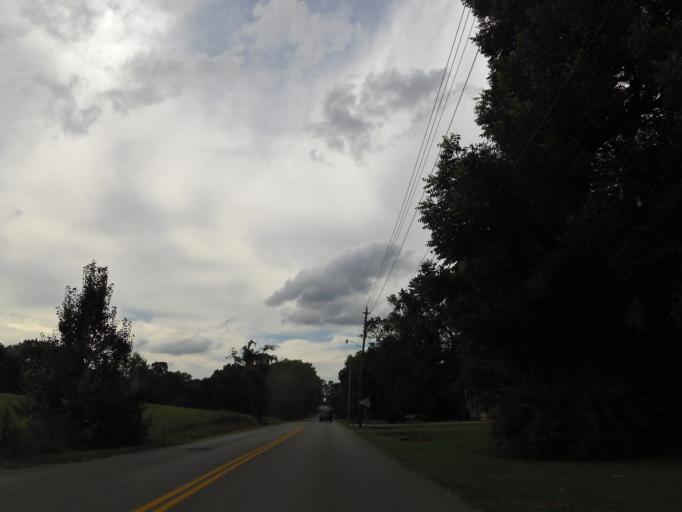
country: US
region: Kentucky
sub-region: Christian County
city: Hopkinsville
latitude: 36.8489
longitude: -87.5127
